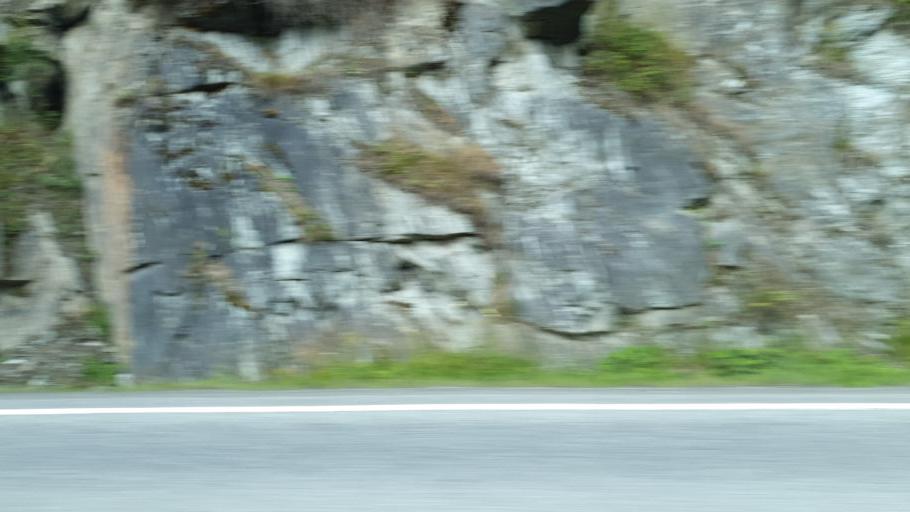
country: NO
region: Sor-Trondelag
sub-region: Midtre Gauldal
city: Storen
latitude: 63.0193
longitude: 10.2466
